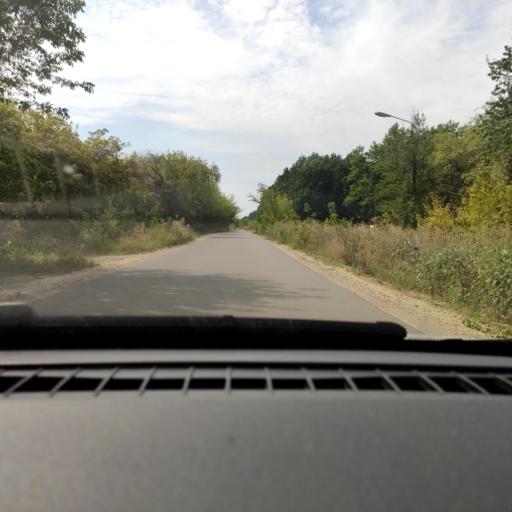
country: RU
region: Voronezj
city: Pridonskoy
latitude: 51.7384
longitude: 39.0670
